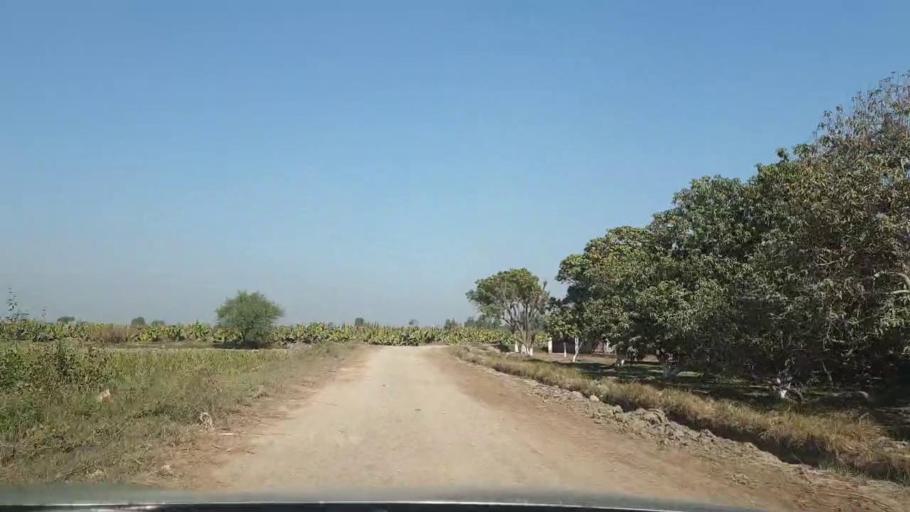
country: PK
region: Sindh
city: Tando Adam
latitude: 25.6236
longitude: 68.6440
